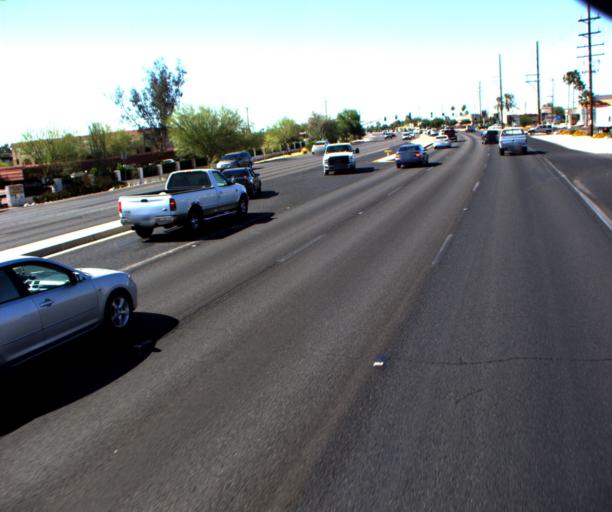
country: US
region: Arizona
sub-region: Pima County
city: Casas Adobes
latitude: 32.3206
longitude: -110.9746
